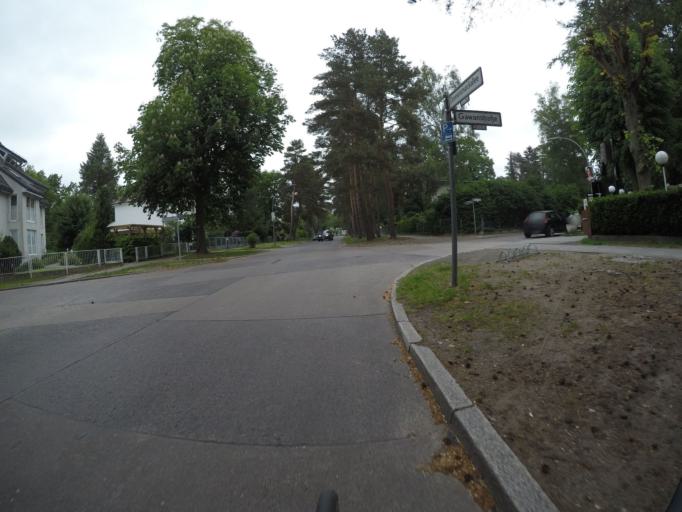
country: DE
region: Berlin
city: Frohnau
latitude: 52.6288
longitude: 13.2775
